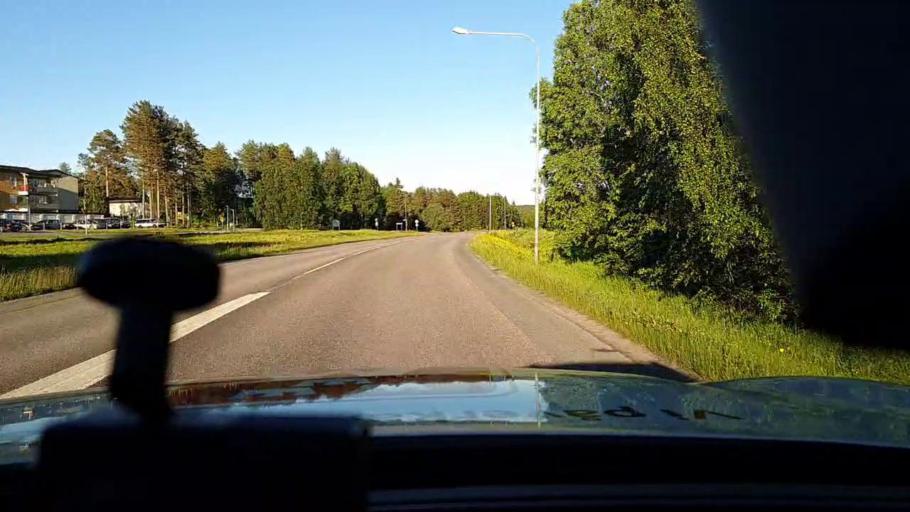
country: SE
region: Norrbotten
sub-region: Lulea Kommun
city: Lulea
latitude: 65.6149
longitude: 22.1501
